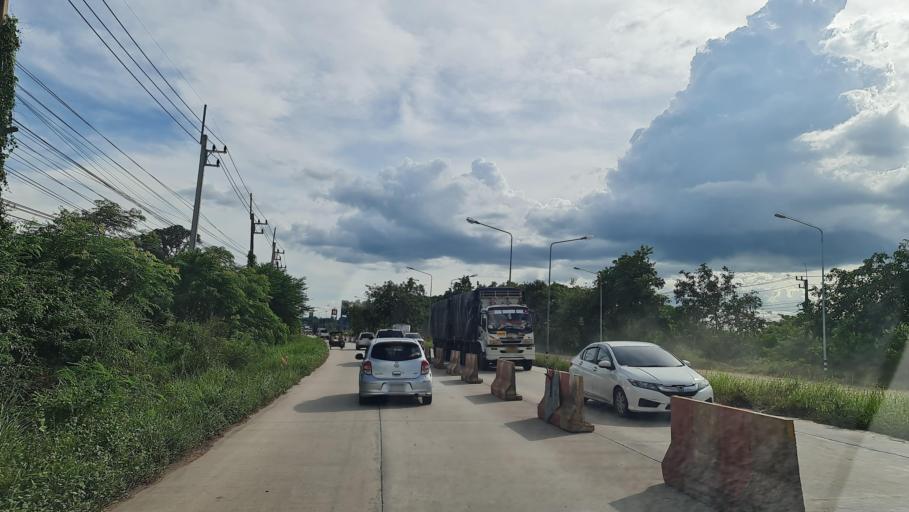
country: TH
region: Khon Kaen
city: Nam Phong
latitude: 16.7494
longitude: 102.8055
